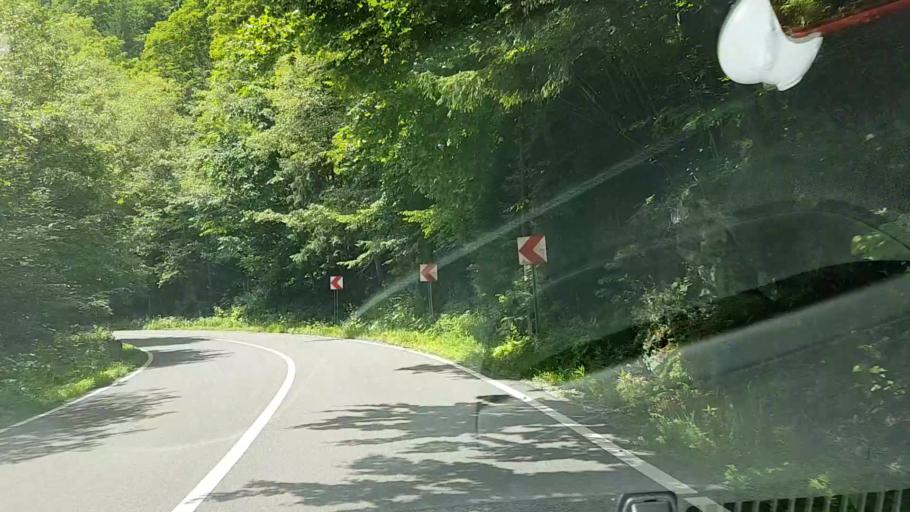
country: RO
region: Suceava
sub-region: Comuna Crucea
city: Crucea
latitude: 47.3111
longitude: 25.6243
